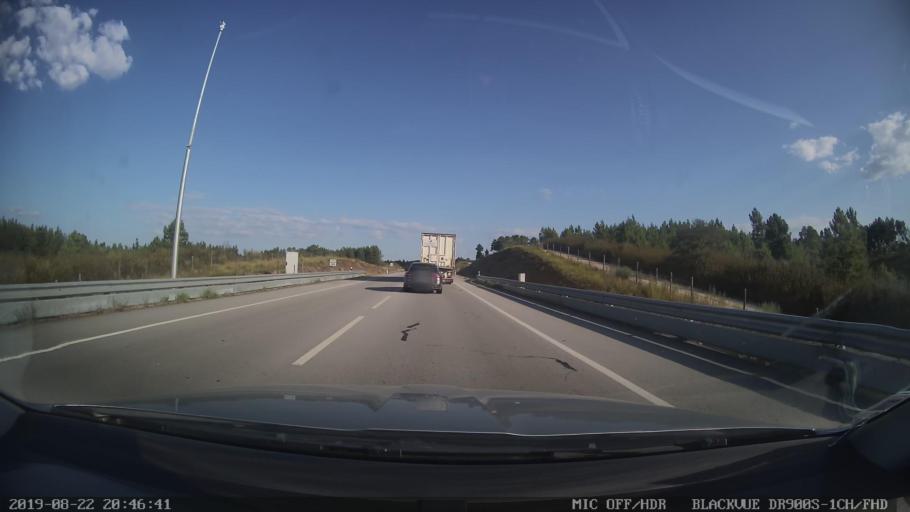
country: PT
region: Castelo Branco
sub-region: Proenca-A-Nova
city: Proenca-a-Nova
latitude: 39.7287
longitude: -7.8787
